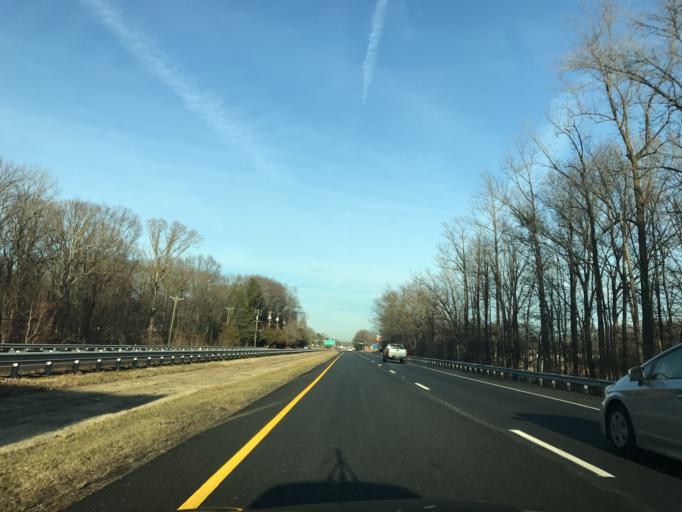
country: US
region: Maryland
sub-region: Cecil County
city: North East
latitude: 39.6009
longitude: -75.9681
